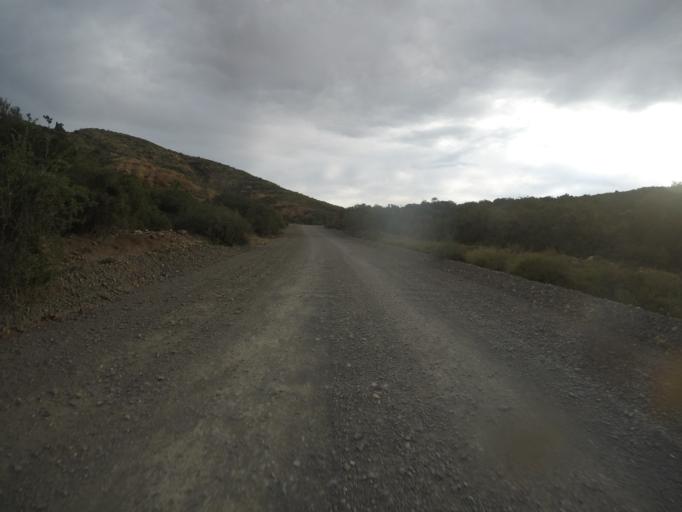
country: ZA
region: Eastern Cape
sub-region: Cacadu District Municipality
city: Willowmore
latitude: -33.5141
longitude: 23.8165
